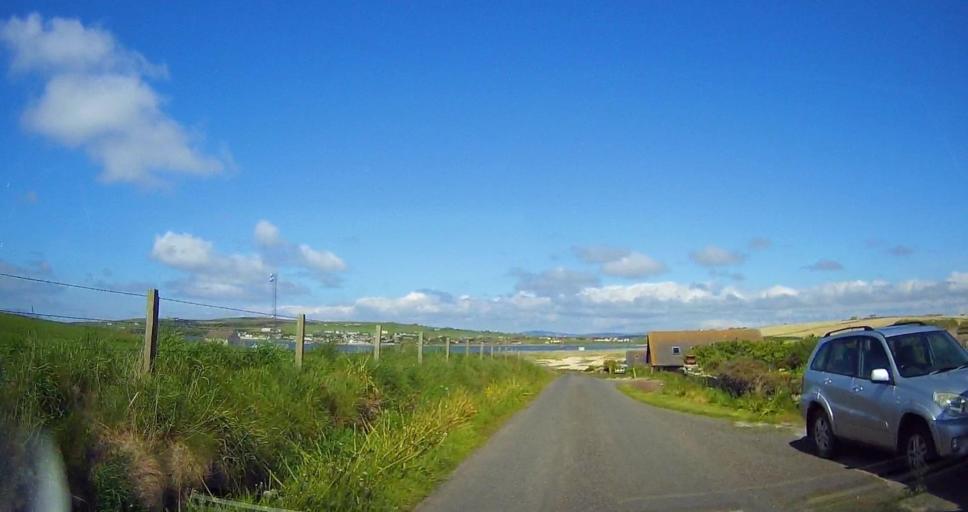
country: GB
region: Scotland
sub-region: Orkney Islands
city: Kirkwall
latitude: 58.8360
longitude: -2.9027
